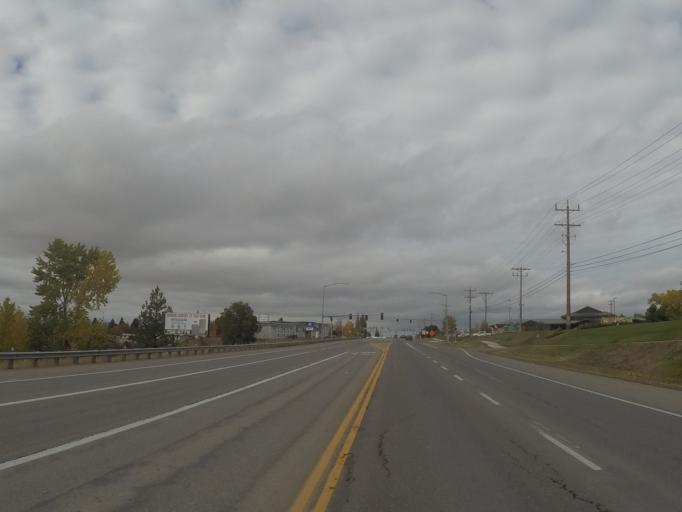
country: US
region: Montana
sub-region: Flathead County
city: Kalispell
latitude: 48.2138
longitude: -114.3281
